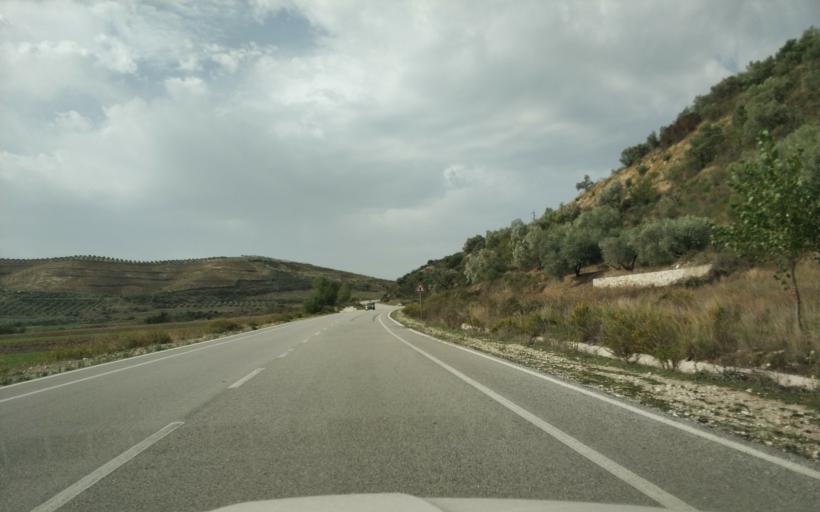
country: AL
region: Gjirokaster
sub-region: Rrethi i Tepelenes
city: Krahes
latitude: 40.3910
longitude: 19.8770
